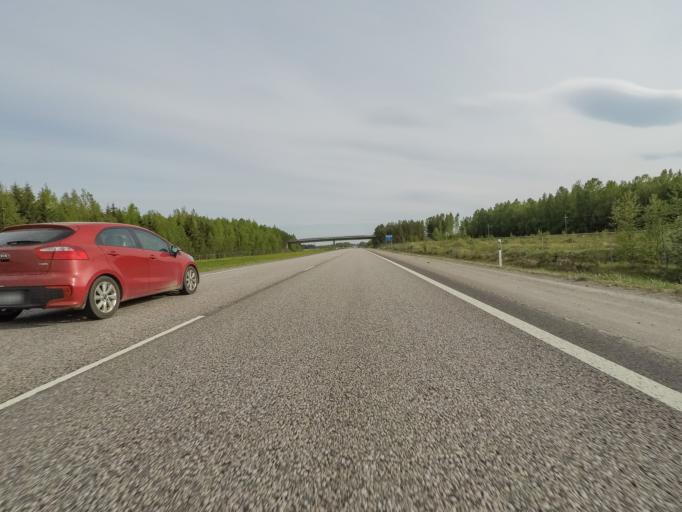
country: FI
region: Uusimaa
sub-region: Helsinki
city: Nurmijaervi
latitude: 60.5348
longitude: 24.8409
